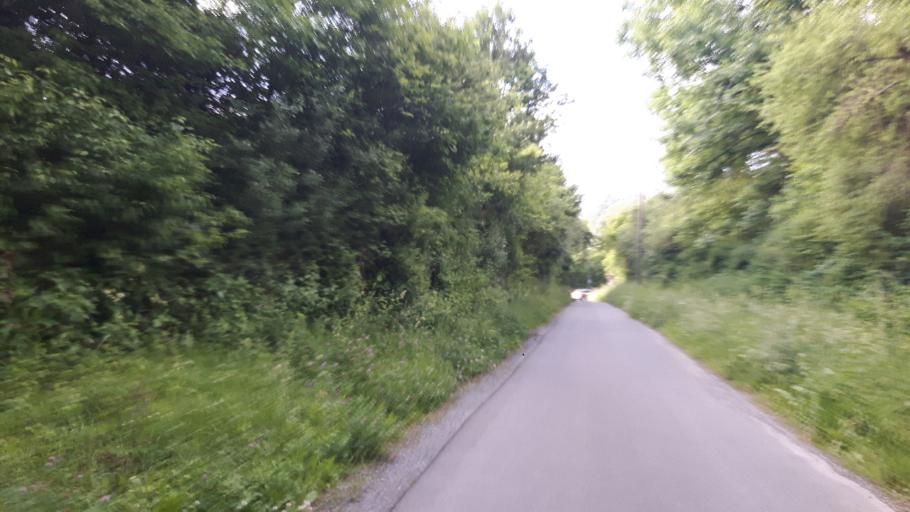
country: DE
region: Bavaria
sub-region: Regierungsbezirk Unterfranken
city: Wuerzburg
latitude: 49.7582
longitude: 9.9421
